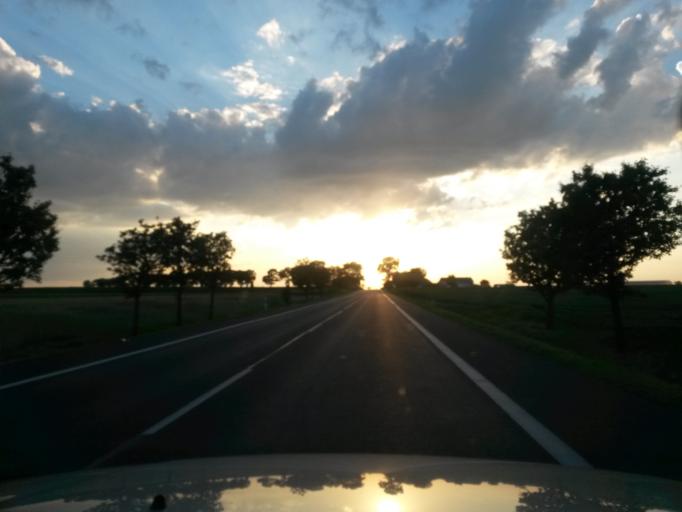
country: PL
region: Lodz Voivodeship
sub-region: Powiat wielunski
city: Czarnozyly
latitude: 51.2499
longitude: 18.5141
